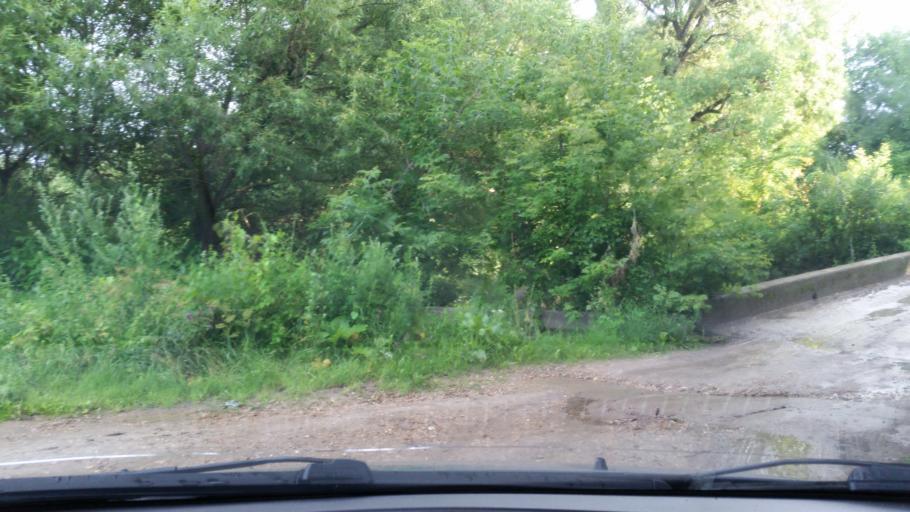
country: RU
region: Moskovskaya
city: Bol'shoye Gryzlovo
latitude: 54.8761
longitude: 37.8215
